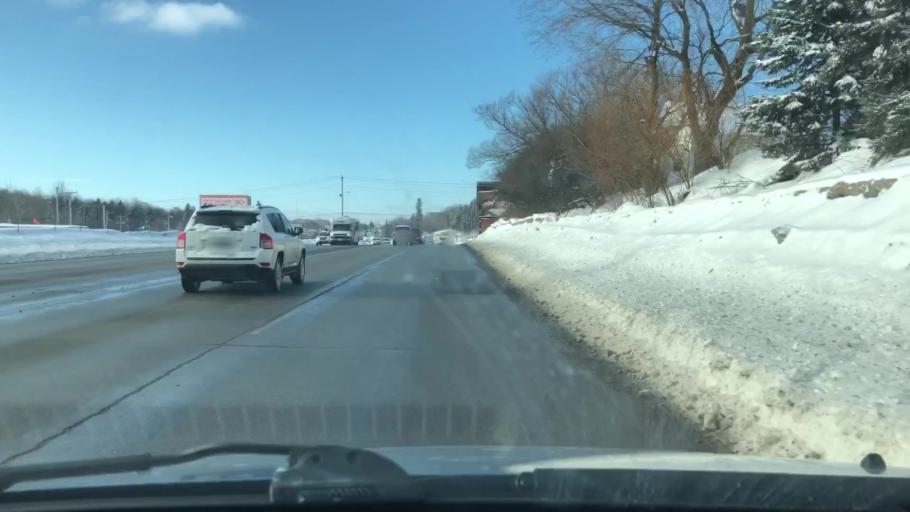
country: US
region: Minnesota
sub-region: Saint Louis County
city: Duluth
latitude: 46.7999
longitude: -92.1196
